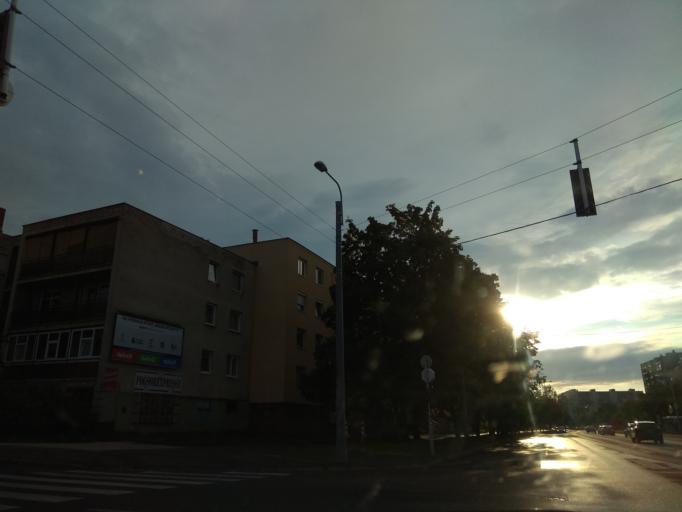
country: HU
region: Borsod-Abauj-Zemplen
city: Miskolc
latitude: 48.0992
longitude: 20.7979
